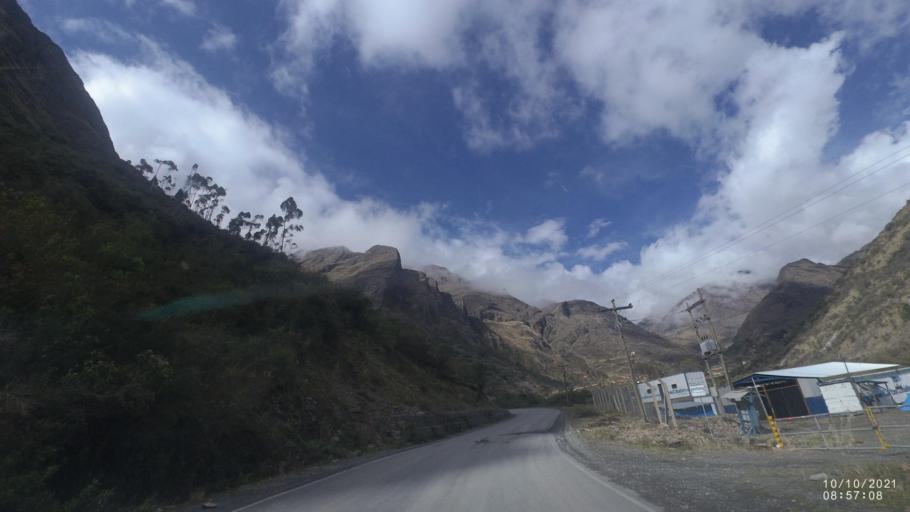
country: BO
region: La Paz
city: Quime
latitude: -16.9928
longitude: -67.2488
